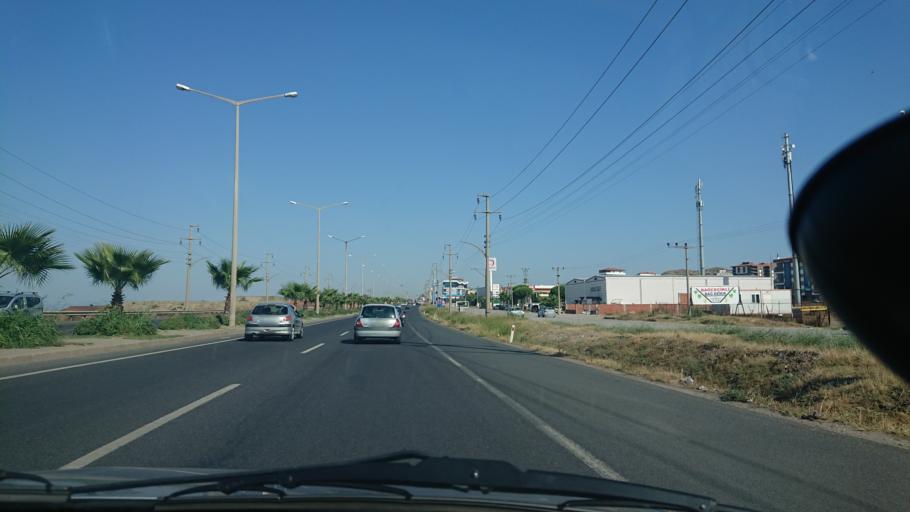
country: TR
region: Manisa
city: Turgutlu
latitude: 38.4957
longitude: 27.7297
